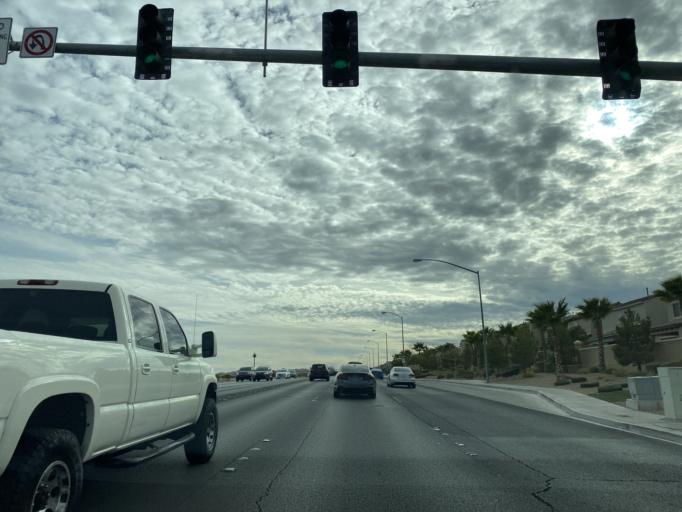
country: US
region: Nevada
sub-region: Clark County
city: Enterprise
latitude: 36.0476
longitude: -115.2792
